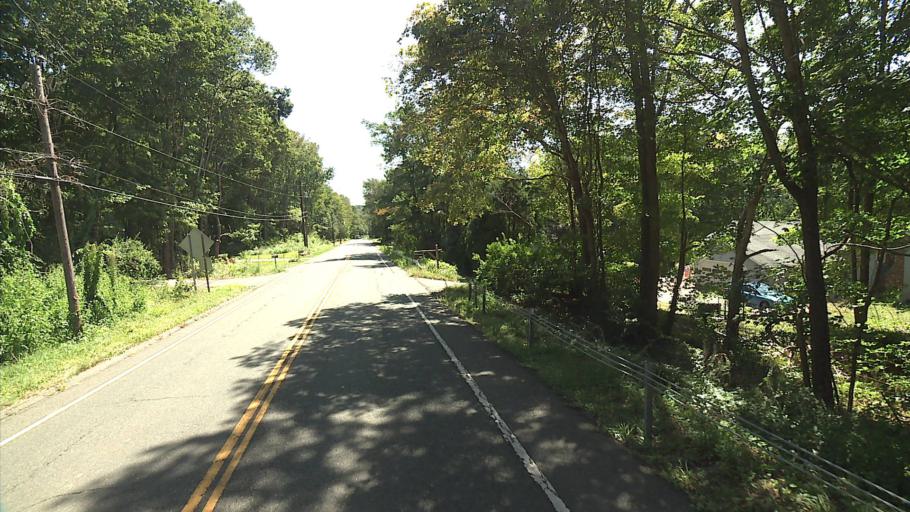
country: US
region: Connecticut
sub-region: New Haven County
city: Southbury
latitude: 41.4704
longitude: -73.1638
